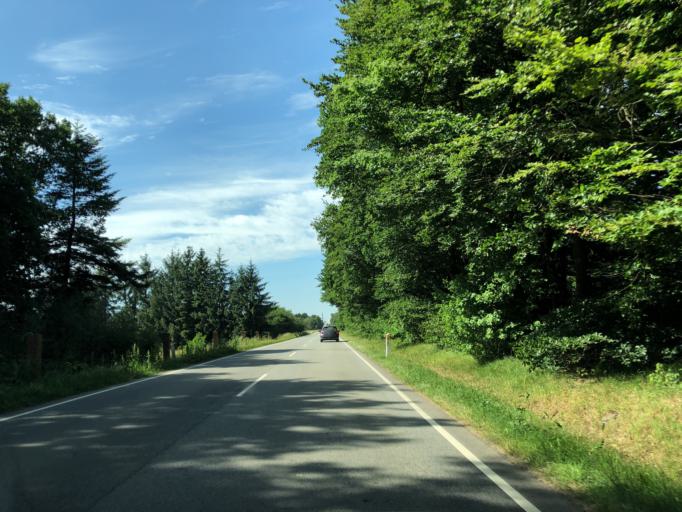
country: DK
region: Central Jutland
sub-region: Ikast-Brande Kommune
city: Brande
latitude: 55.9213
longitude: 9.1648
